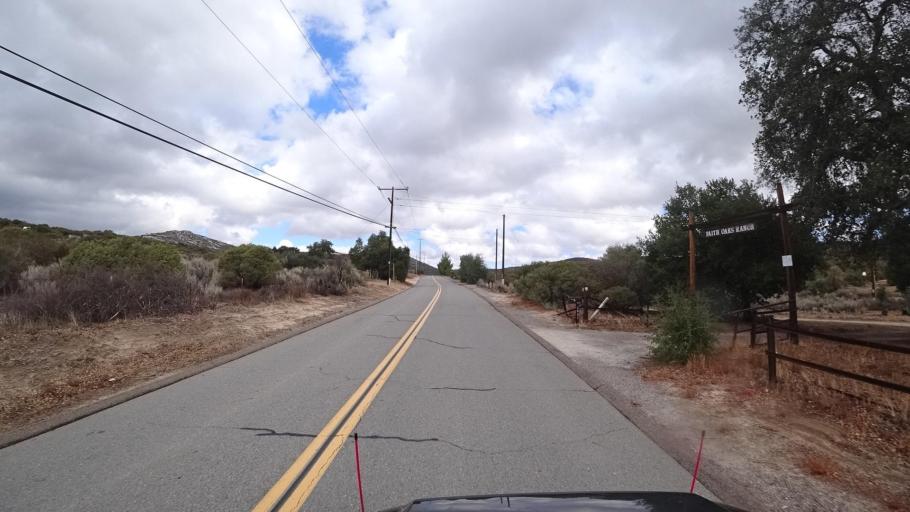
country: US
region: California
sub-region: San Diego County
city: Campo
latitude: 32.6553
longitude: -116.4250
